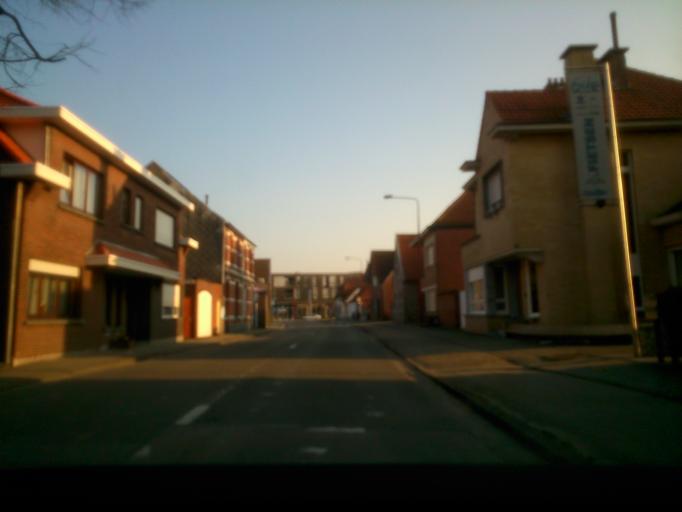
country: BE
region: Flanders
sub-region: Provincie Antwerpen
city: Stabroek
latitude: 51.3320
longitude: 4.3622
